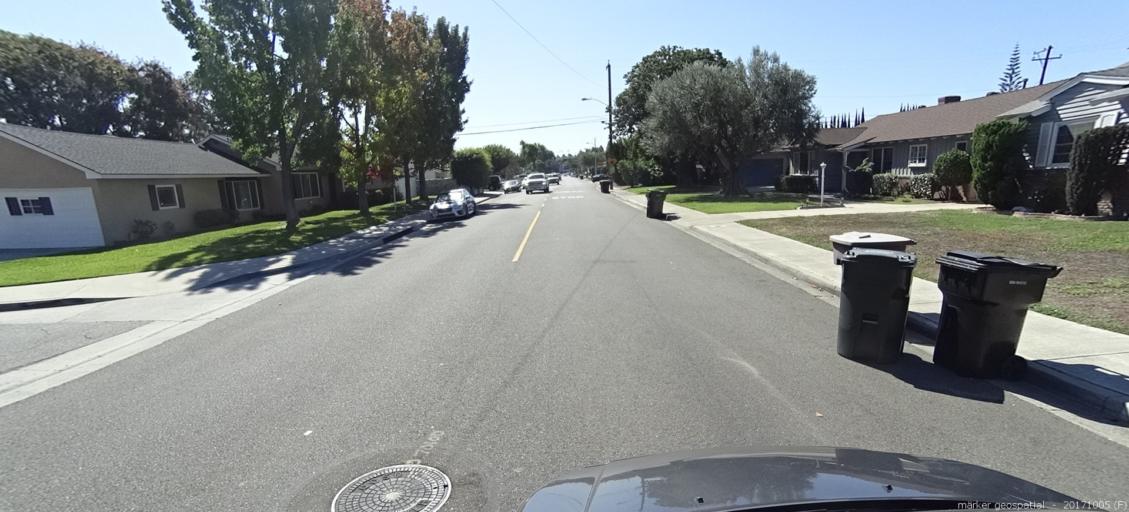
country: US
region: California
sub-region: Orange County
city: Garden Grove
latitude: 33.7709
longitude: -117.9676
